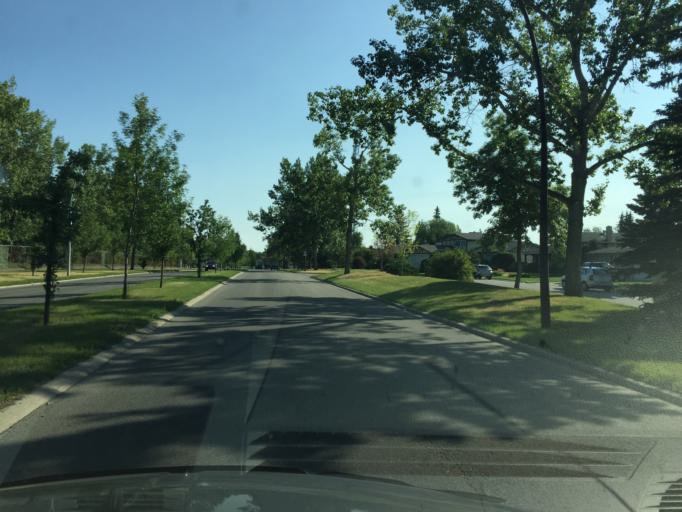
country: CA
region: Alberta
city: Calgary
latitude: 50.9399
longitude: -114.0468
